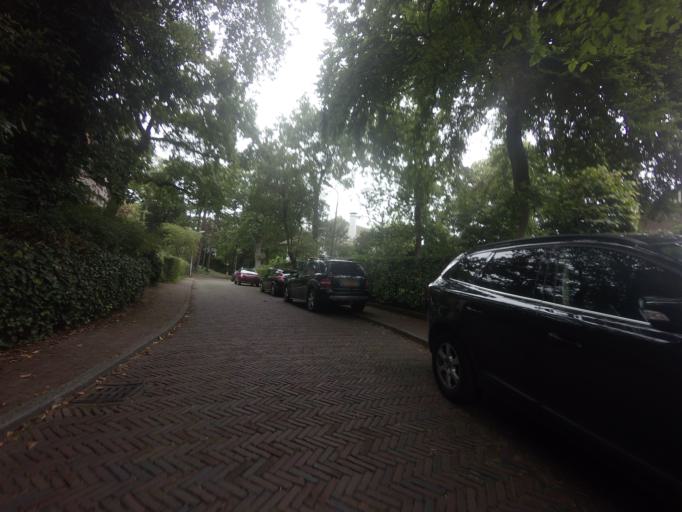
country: NL
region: North Holland
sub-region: Gemeente Bloemendaal
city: Bloemendaal
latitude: 52.4181
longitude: 4.6268
